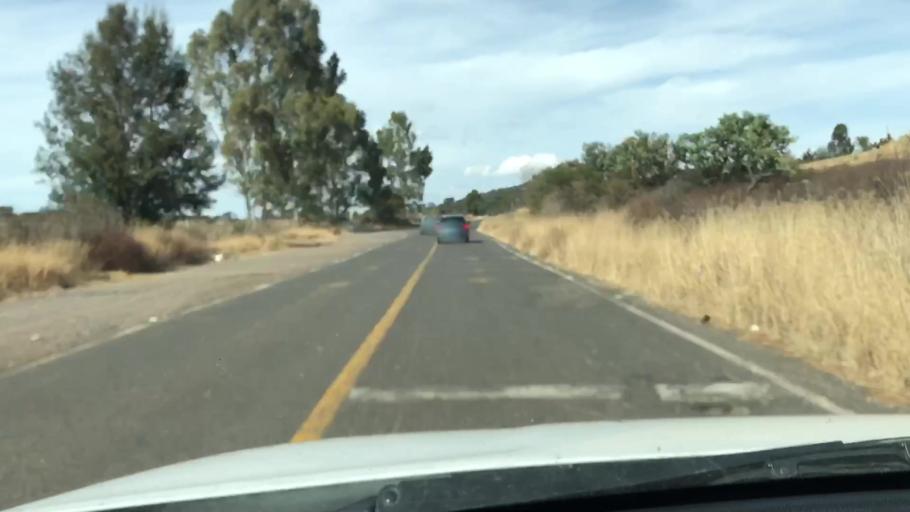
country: MX
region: Jalisco
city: Chiquilistlan
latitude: 20.1860
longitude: -103.7246
